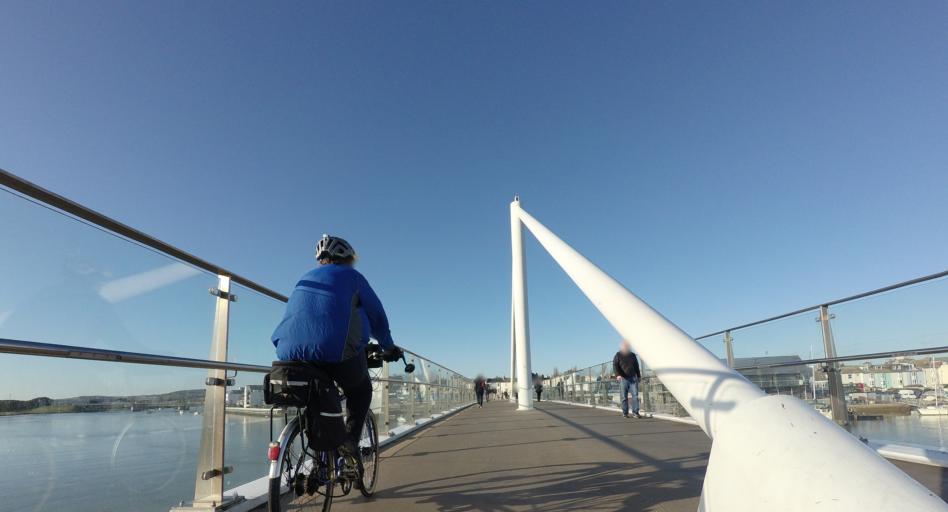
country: GB
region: England
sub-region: West Sussex
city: Shoreham-by-Sea
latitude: 50.8305
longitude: -0.2738
